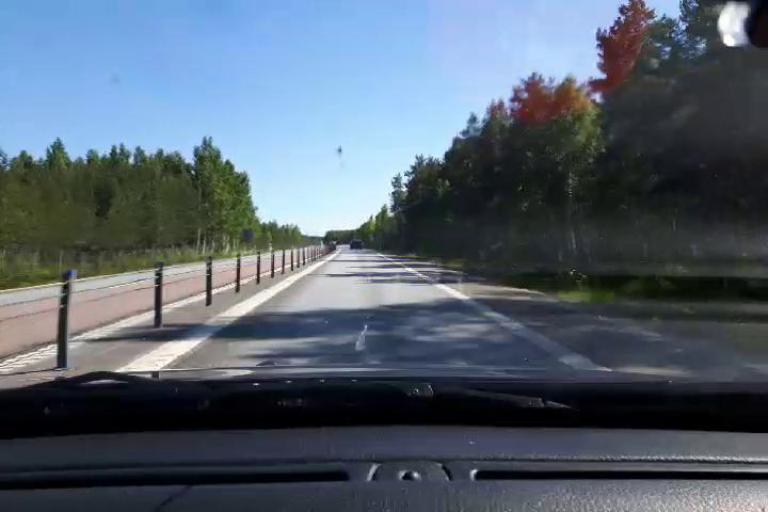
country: SE
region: Gaevleborg
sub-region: Gavle Kommun
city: Norrsundet
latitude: 60.8390
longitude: 17.0773
